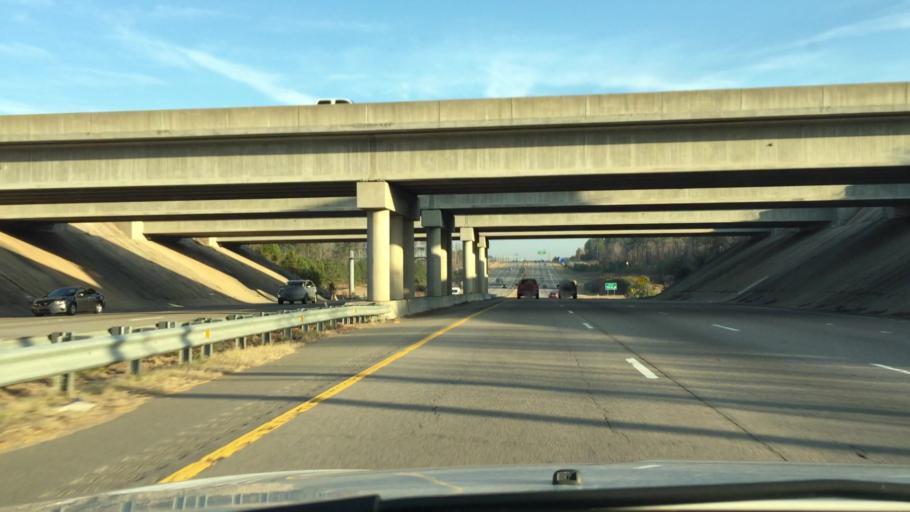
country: US
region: North Carolina
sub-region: Lee County
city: Sanford
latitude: 35.5105
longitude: -79.1881
